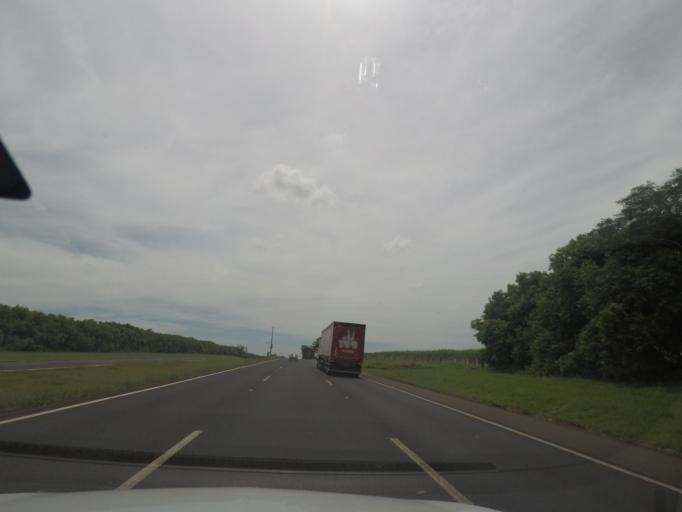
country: BR
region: Sao Paulo
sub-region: Bebedouro
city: Bebedouro
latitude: -20.9899
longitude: -48.4338
